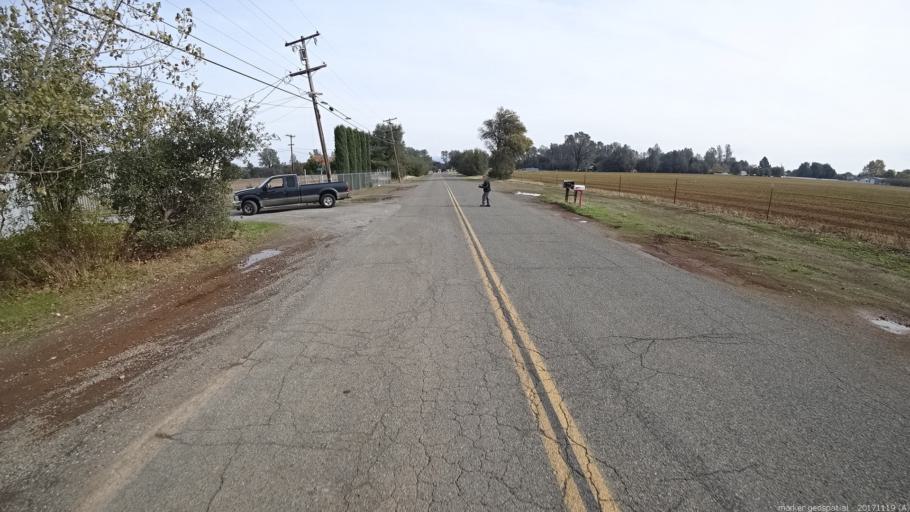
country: US
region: California
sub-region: Shasta County
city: Anderson
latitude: 40.4913
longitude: -122.2774
